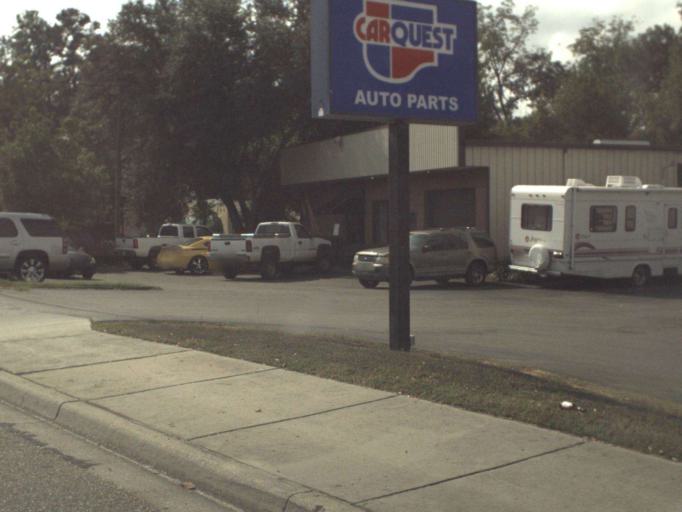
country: US
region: Florida
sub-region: Leon County
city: Tallahassee
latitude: 30.4677
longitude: -84.2305
